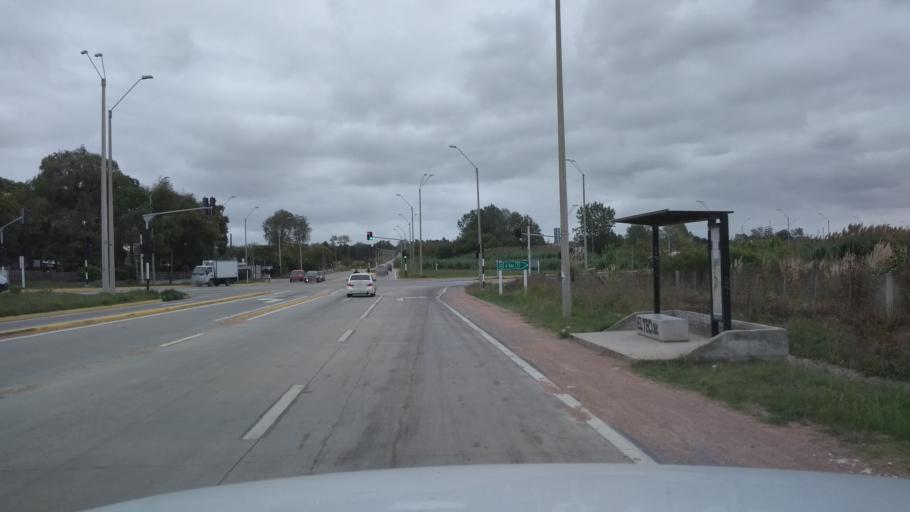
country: UY
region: Canelones
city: Toledo
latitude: -34.7965
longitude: -56.1520
